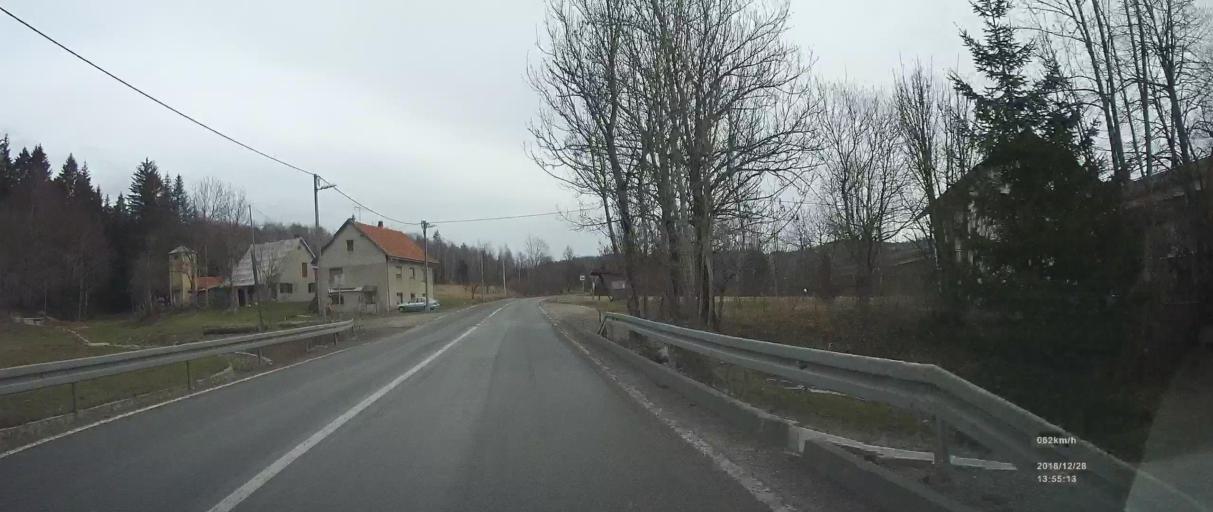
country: HR
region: Primorsko-Goranska
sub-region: Grad Delnice
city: Delnice
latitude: 45.3826
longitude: 14.8729
